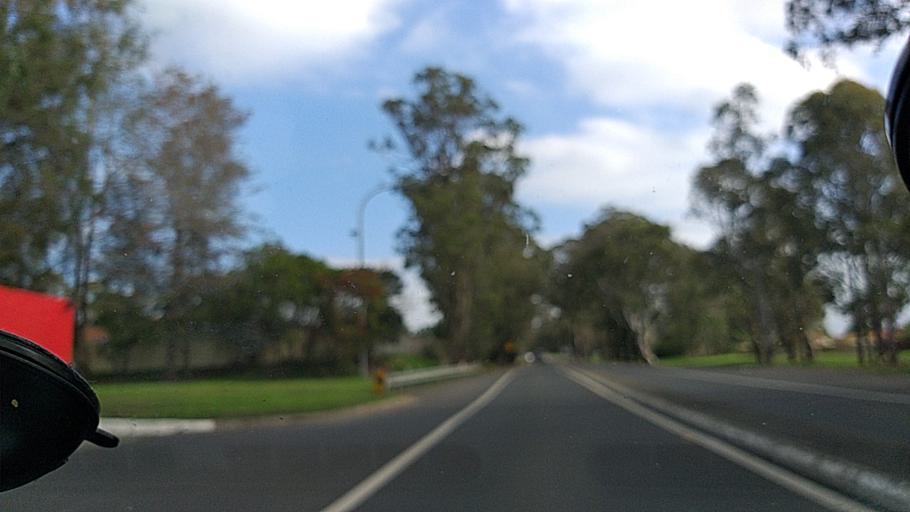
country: AU
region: New South Wales
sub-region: Campbelltown Municipality
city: Glen Alpine
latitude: -34.1119
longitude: 150.7983
